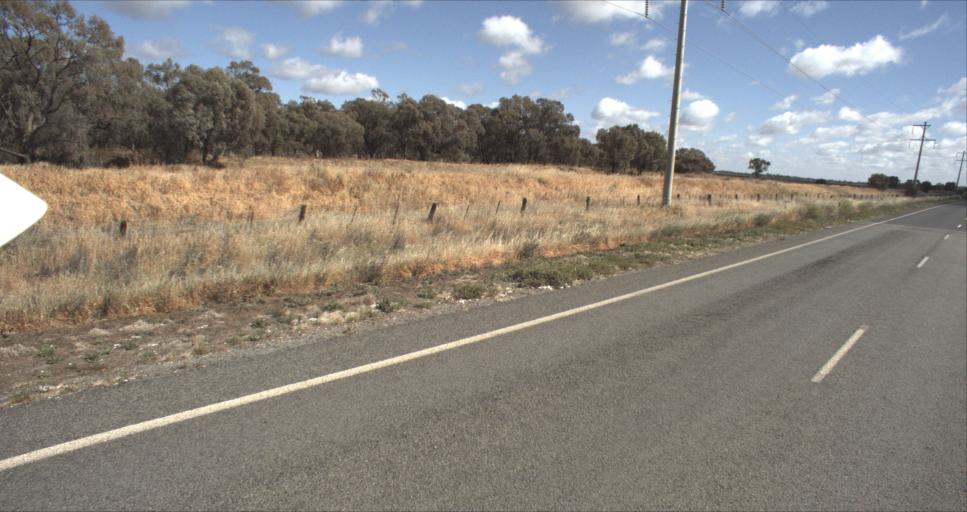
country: AU
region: New South Wales
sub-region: Murrumbidgee Shire
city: Darlington Point
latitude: -34.5443
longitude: 146.1716
